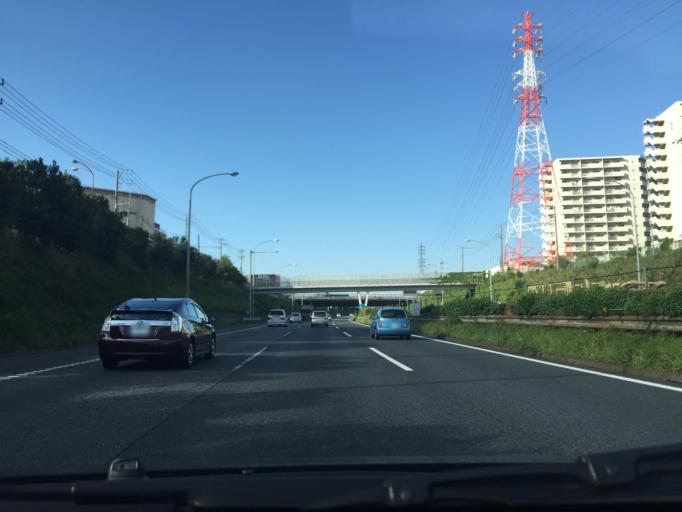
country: JP
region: Kanagawa
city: Minami-rinkan
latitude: 35.4962
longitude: 139.4738
